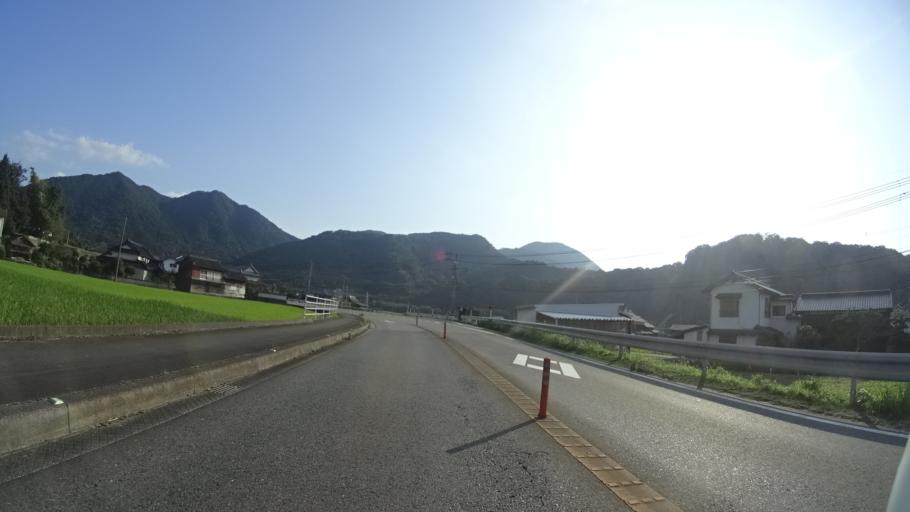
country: JP
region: Oita
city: Bungo-Takada-shi
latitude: 33.4995
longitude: 131.3254
